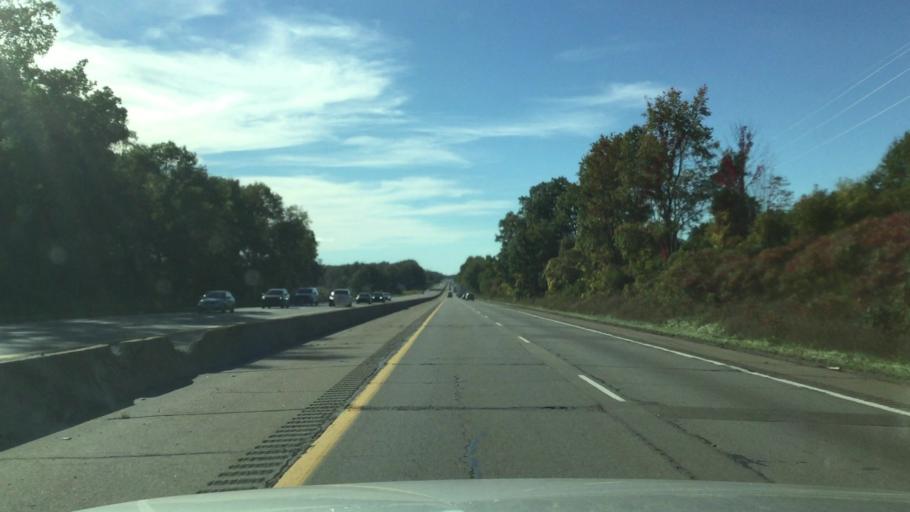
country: US
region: Michigan
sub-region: Jackson County
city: Spring Arbor
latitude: 42.2691
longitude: -84.5546
